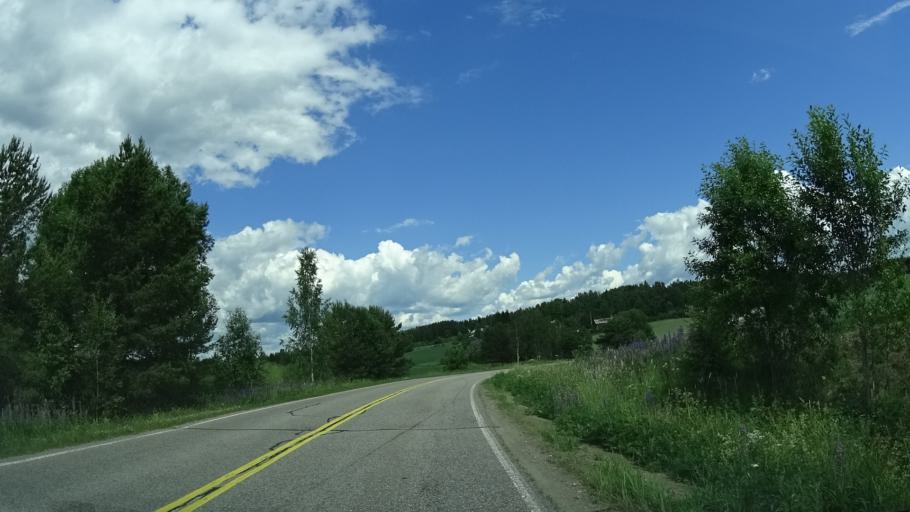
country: FI
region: Uusimaa
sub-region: Helsinki
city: Espoo
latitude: 60.3804
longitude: 24.6440
